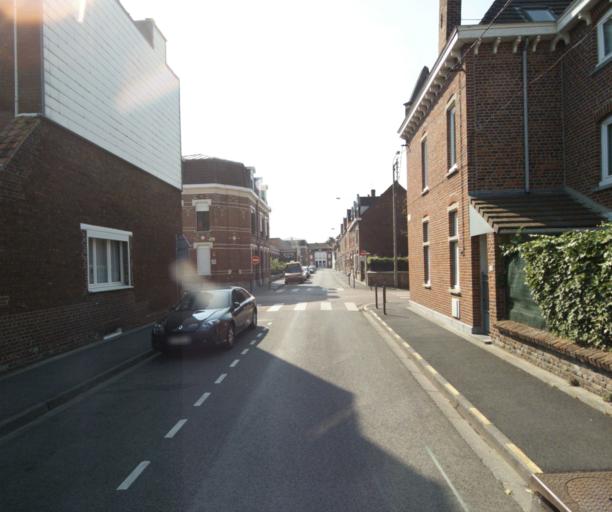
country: FR
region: Nord-Pas-de-Calais
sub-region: Departement du Nord
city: Comines
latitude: 50.7634
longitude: 3.0075
